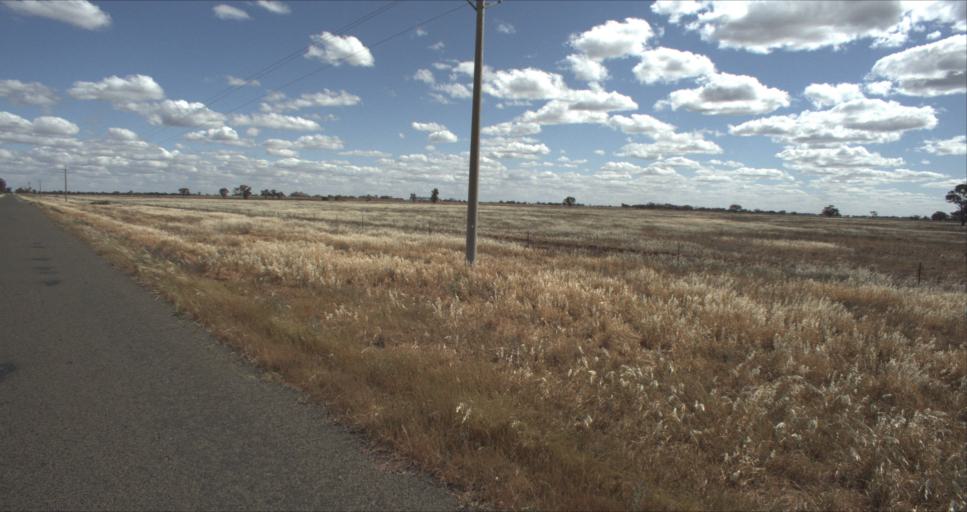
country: AU
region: New South Wales
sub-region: Leeton
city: Leeton
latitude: -34.4667
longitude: 146.2517
